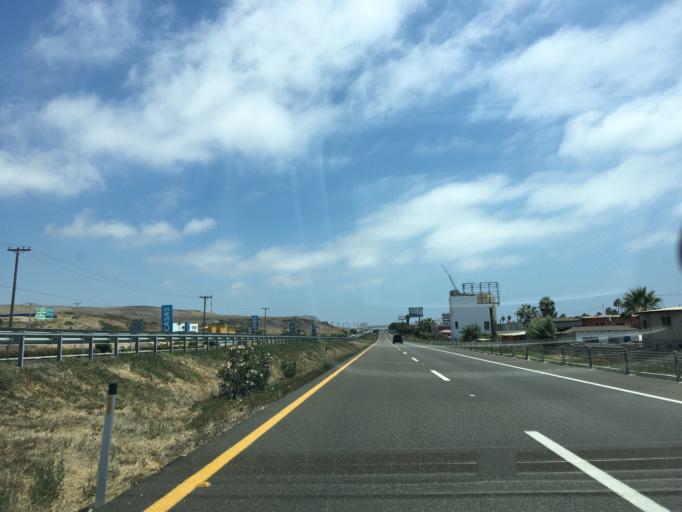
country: MX
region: Baja California
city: Rosarito
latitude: 32.3201
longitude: -117.0481
